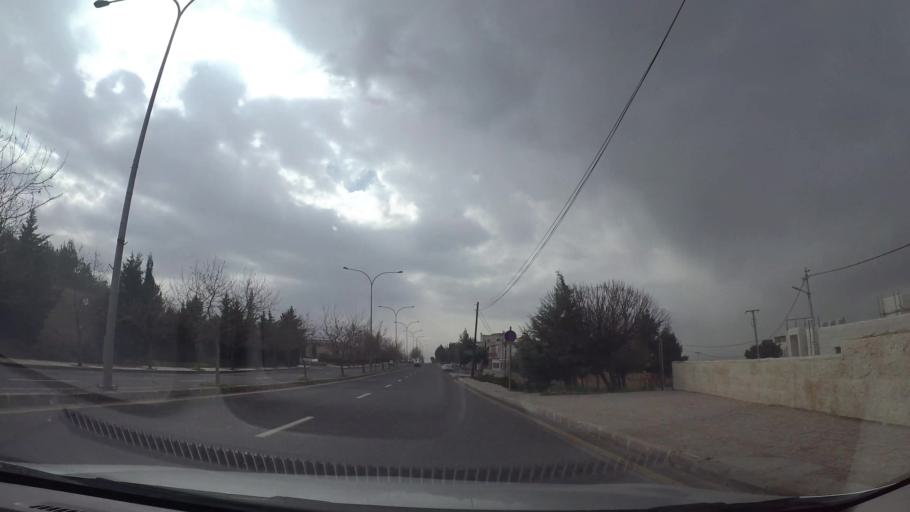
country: JO
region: Amman
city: Wadi as Sir
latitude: 31.9827
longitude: 35.8213
